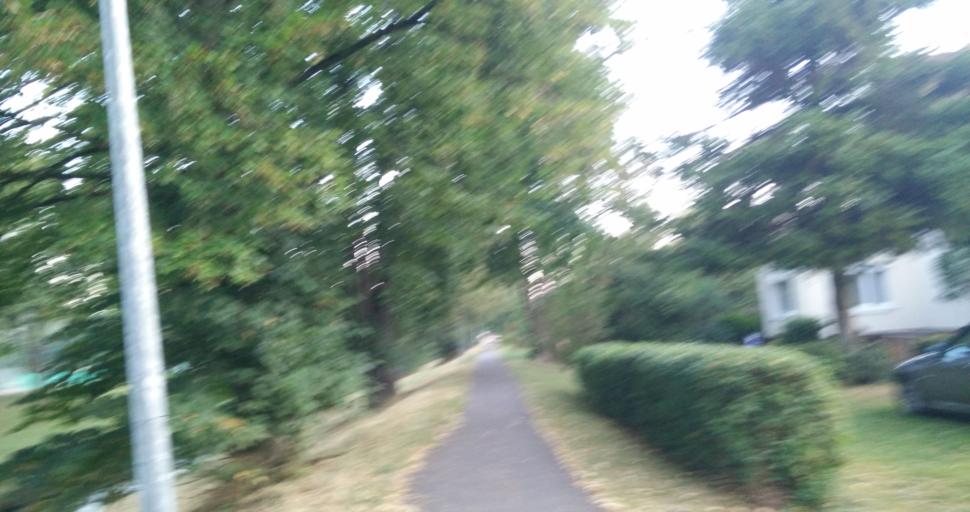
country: DE
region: Baden-Wuerttemberg
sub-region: Tuebingen Region
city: Tuebingen
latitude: 48.4945
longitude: 9.0641
